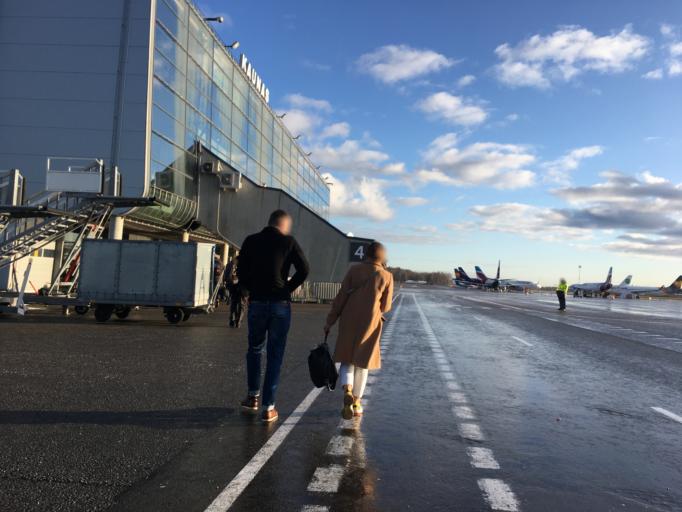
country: LT
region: Kauno apskritis
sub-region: Kauno rajonas
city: Karmelava
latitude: 54.9666
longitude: 24.0731
